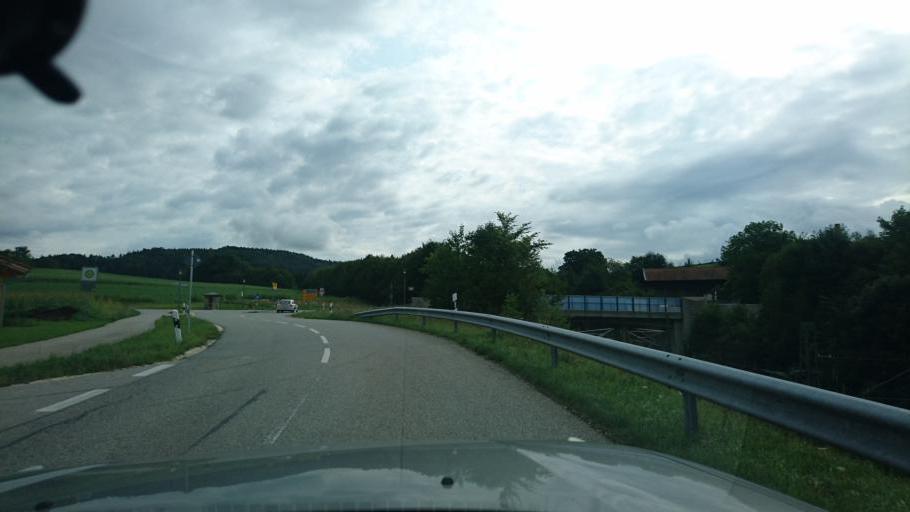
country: DE
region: Bavaria
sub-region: Upper Bavaria
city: Bergen
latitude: 47.8259
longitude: 12.5962
